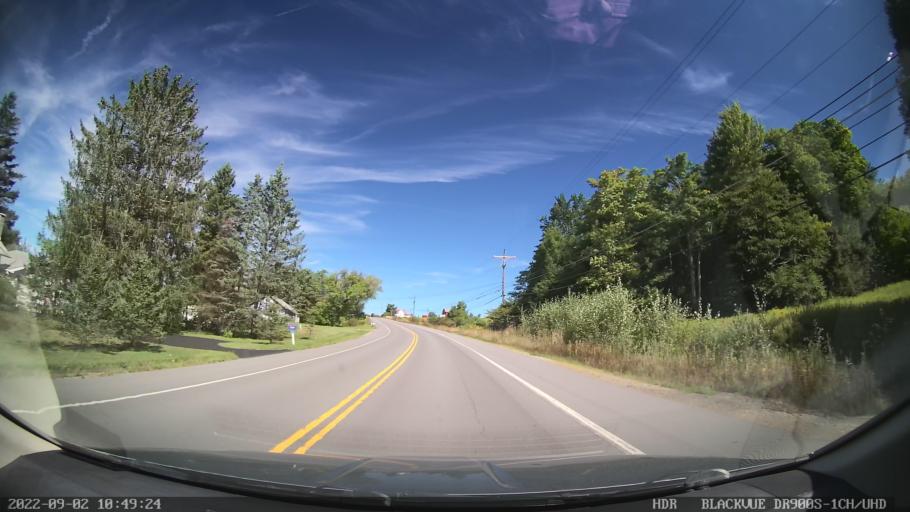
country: US
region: Pennsylvania
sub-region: Tioga County
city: Blossburg
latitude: 41.5998
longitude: -77.1111
